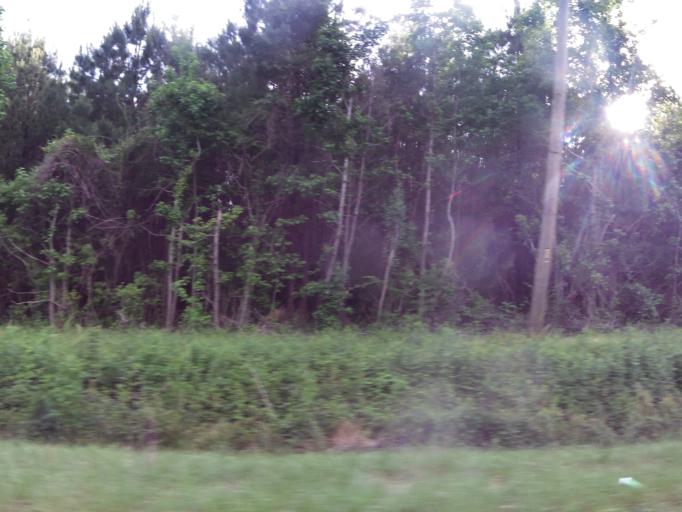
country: US
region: South Carolina
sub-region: Jasper County
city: Ridgeland
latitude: 32.5156
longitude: -81.1449
